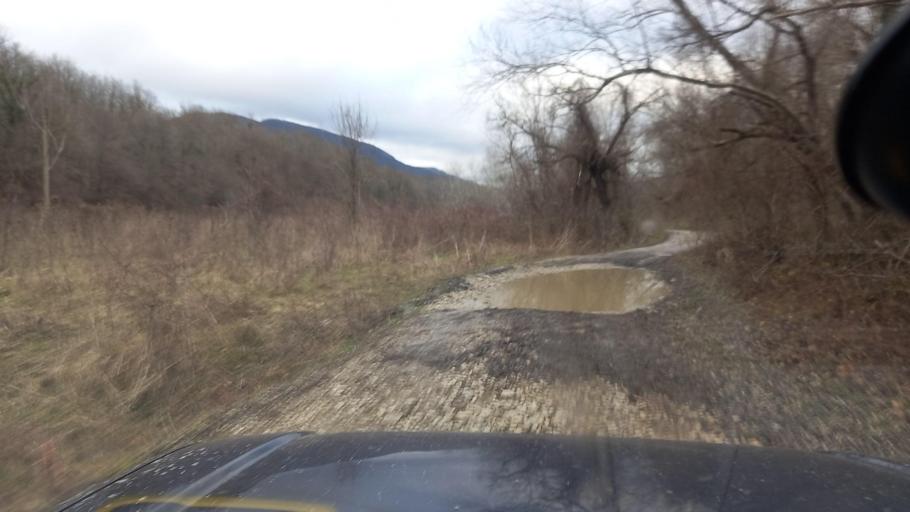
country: RU
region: Krasnodarskiy
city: Pshada
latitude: 44.4880
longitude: 38.4089
